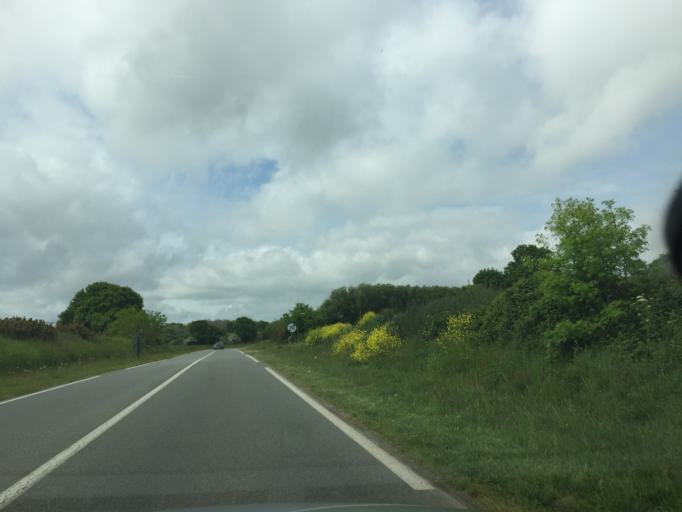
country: FR
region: Brittany
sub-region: Departement des Cotes-d'Armor
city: Saint-Cast-le-Guildo
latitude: 48.6012
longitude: -2.2418
